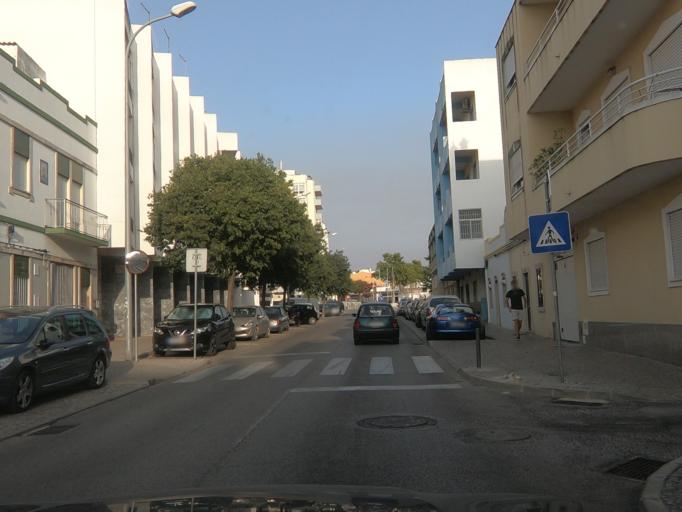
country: PT
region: Faro
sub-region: Loule
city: Loule
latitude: 37.1357
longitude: -8.0142
